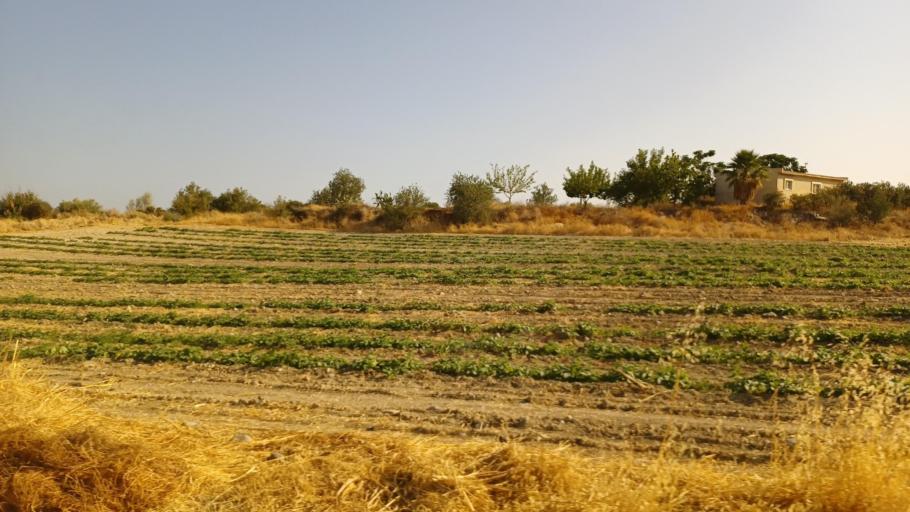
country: CY
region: Pafos
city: Polis
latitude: 35.0545
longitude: 32.4751
